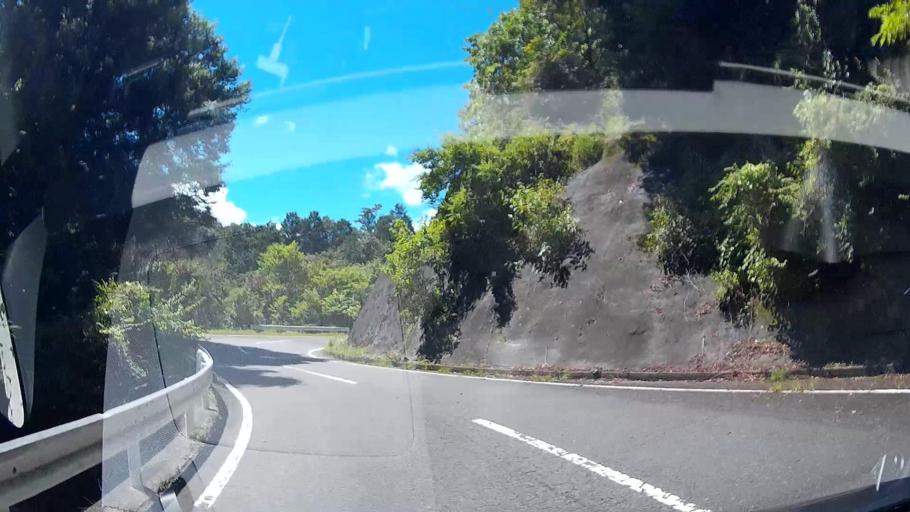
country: JP
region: Shizuoka
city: Shizuoka-shi
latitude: 35.1758
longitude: 138.2975
